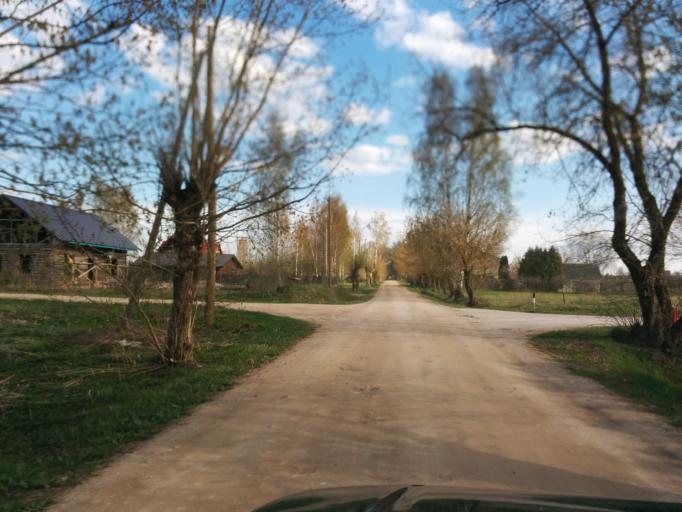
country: LV
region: Jelgava
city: Jelgava
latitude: 56.6630
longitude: 23.6645
